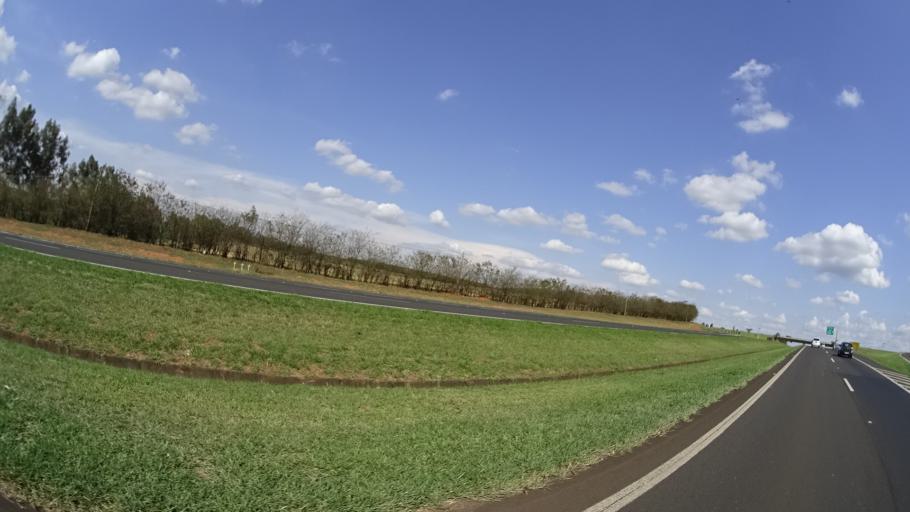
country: BR
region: Sao Paulo
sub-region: Sao Jose Do Rio Preto
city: Sao Jose do Rio Preto
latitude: -20.9037
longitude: -49.2967
